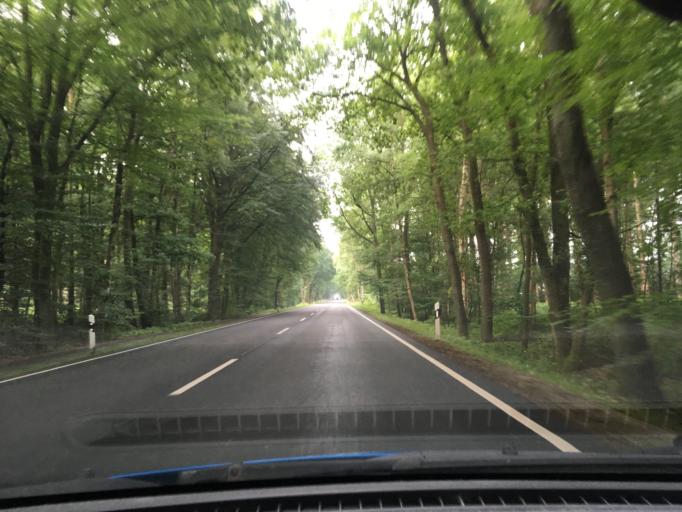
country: DE
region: Lower Saxony
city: Wenzendorf
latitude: 53.3547
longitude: 9.8081
